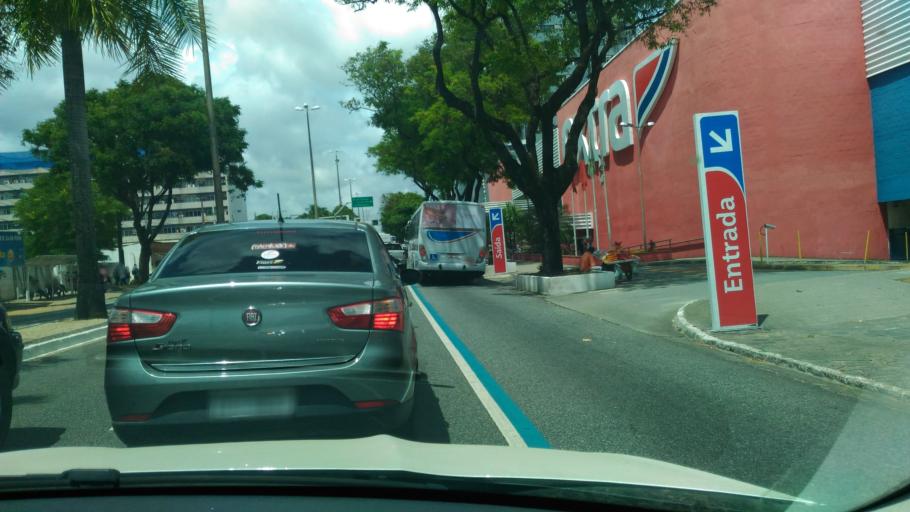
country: BR
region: Paraiba
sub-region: Joao Pessoa
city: Joao Pessoa
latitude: -7.1197
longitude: -34.8579
